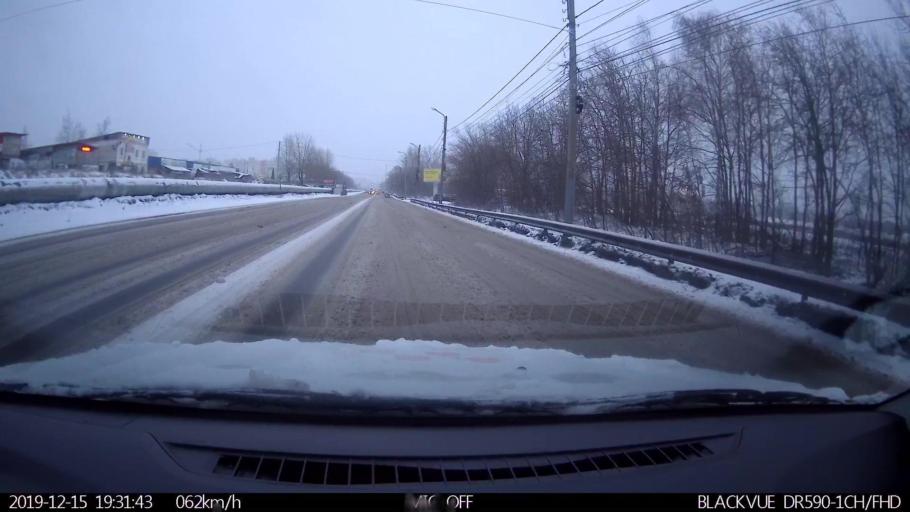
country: RU
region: Nizjnij Novgorod
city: Nizhniy Novgorod
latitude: 56.3434
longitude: 43.8969
